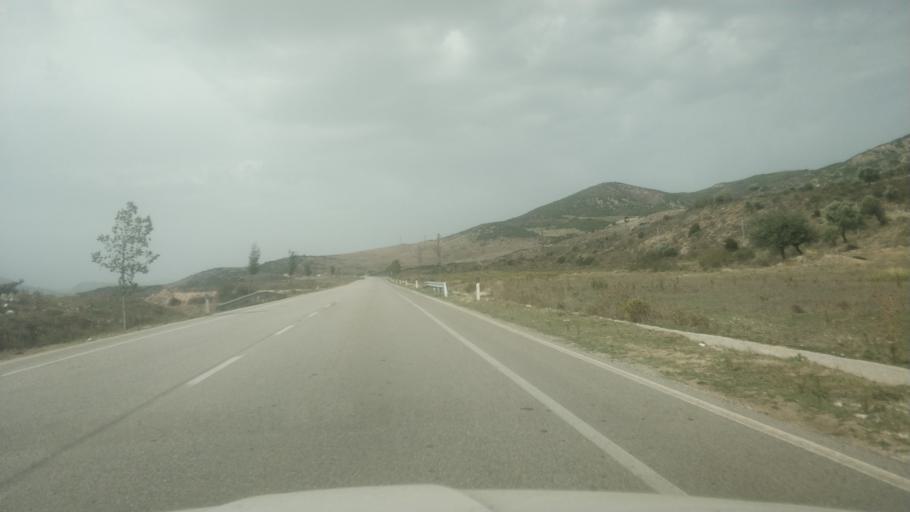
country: AL
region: Gjirokaster
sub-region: Rrethi i Tepelenes
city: Memaliaj
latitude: 40.3585
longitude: 19.9321
